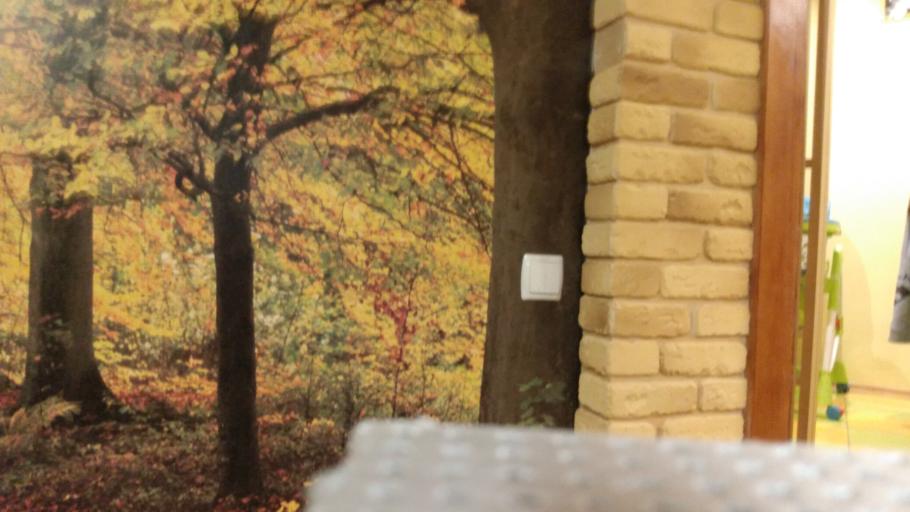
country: RU
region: Vologda
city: Babayevo
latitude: 59.3742
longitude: 35.9921
